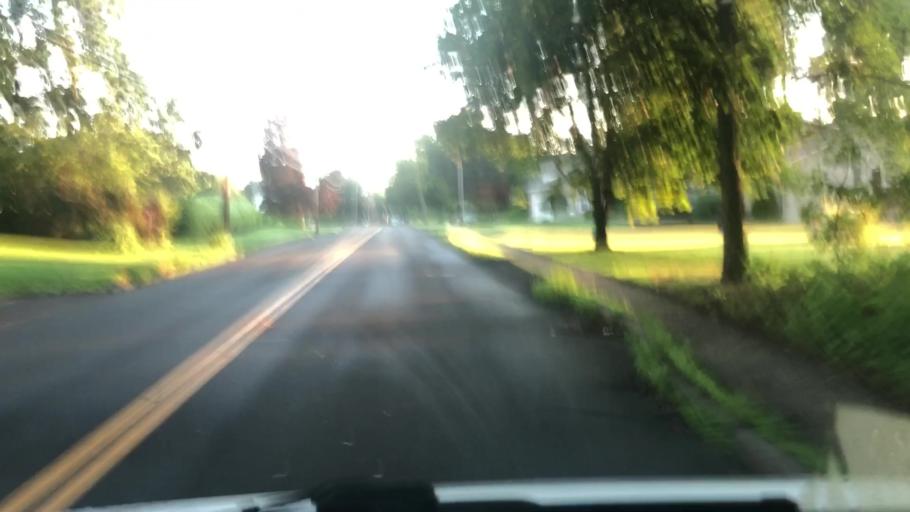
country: US
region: Massachusetts
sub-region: Hampshire County
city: Easthampton
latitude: 42.2705
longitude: -72.6683
